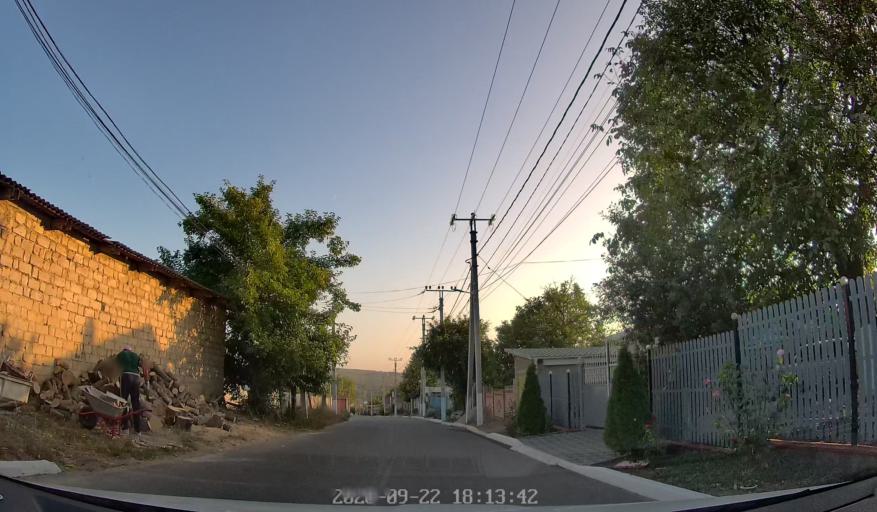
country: MD
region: Laloveni
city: Ialoveni
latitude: 46.9430
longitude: 28.7884
